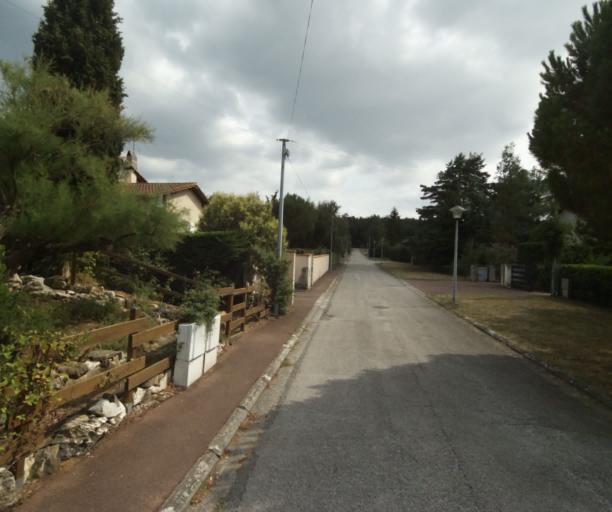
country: FR
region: Midi-Pyrenees
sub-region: Departement de la Haute-Garonne
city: Revel
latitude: 43.4331
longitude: 2.0212
